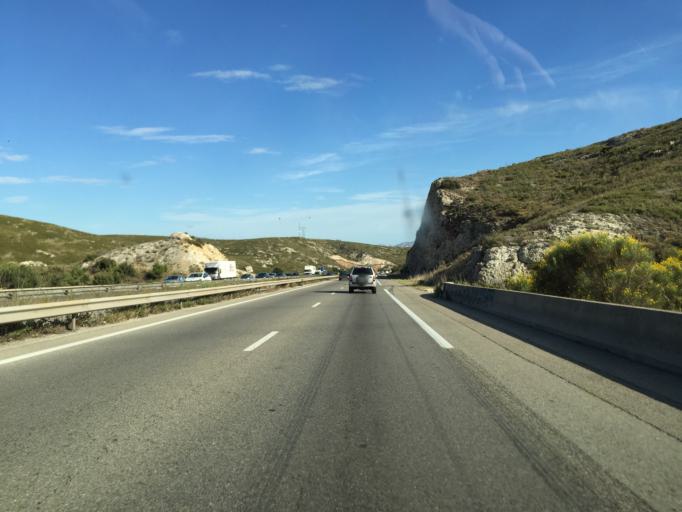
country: FR
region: Provence-Alpes-Cote d'Azur
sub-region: Departement des Bouches-du-Rhone
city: Marseille 16
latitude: 43.3784
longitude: 5.3171
